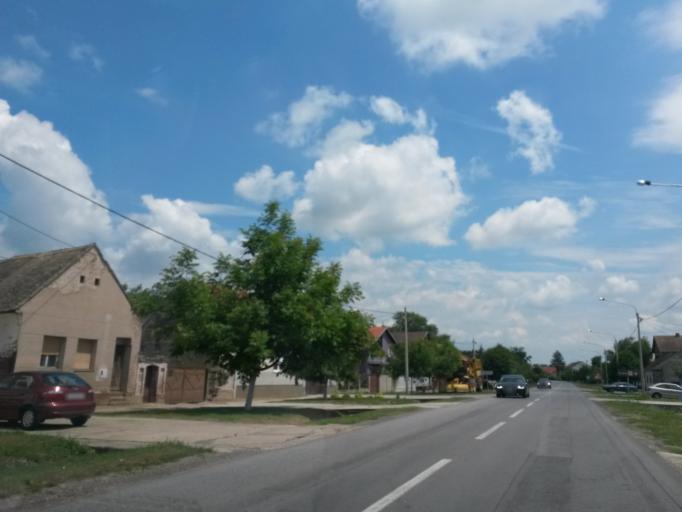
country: HR
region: Osjecko-Baranjska
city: Sarvas
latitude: 45.5165
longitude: 18.8797
